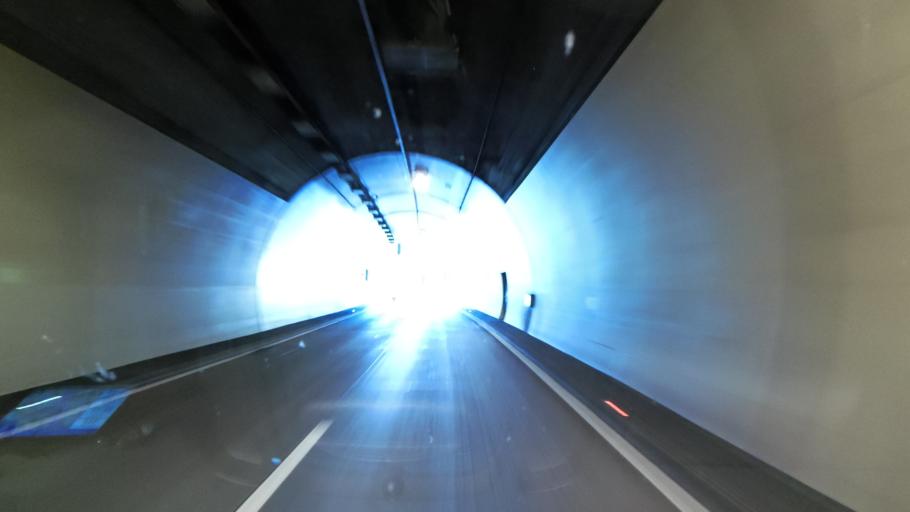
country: AT
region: Carinthia
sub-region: Politischer Bezirk Spittal an der Drau
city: Seeboden
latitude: 46.8045
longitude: 13.5205
